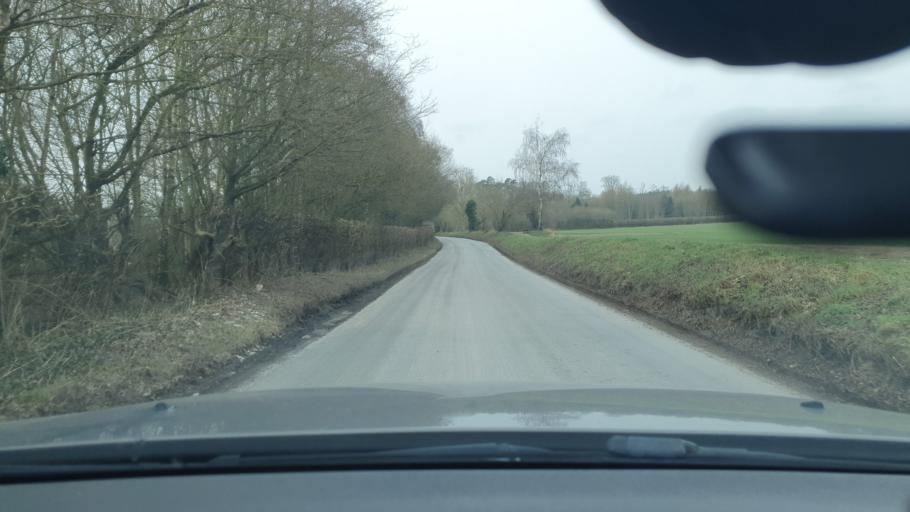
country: GB
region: England
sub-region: Wiltshire
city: Ramsbury
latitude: 51.4404
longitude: -1.6180
